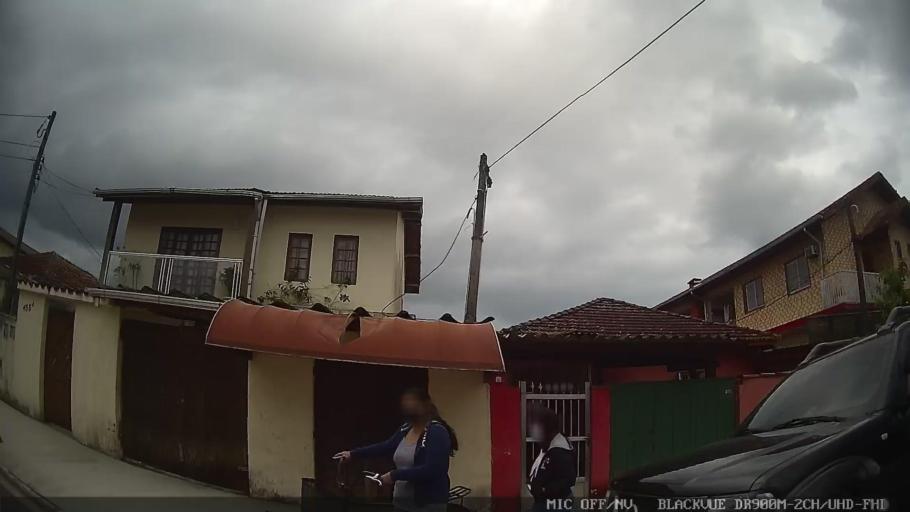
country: BR
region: Sao Paulo
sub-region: Guaruja
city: Guaruja
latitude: -23.9947
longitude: -46.2830
